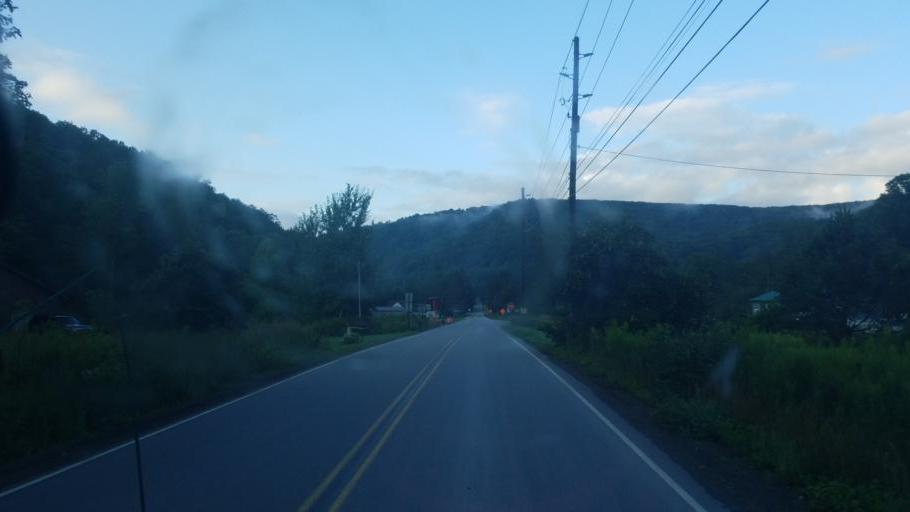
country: US
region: Pennsylvania
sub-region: Potter County
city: Galeton
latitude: 41.8331
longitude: -77.7965
